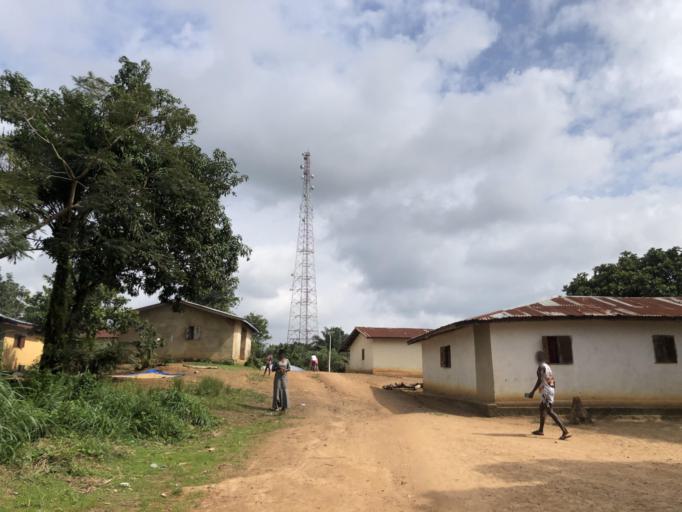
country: SL
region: Eastern Province
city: Kailahun
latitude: 8.2828
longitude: -10.5651
